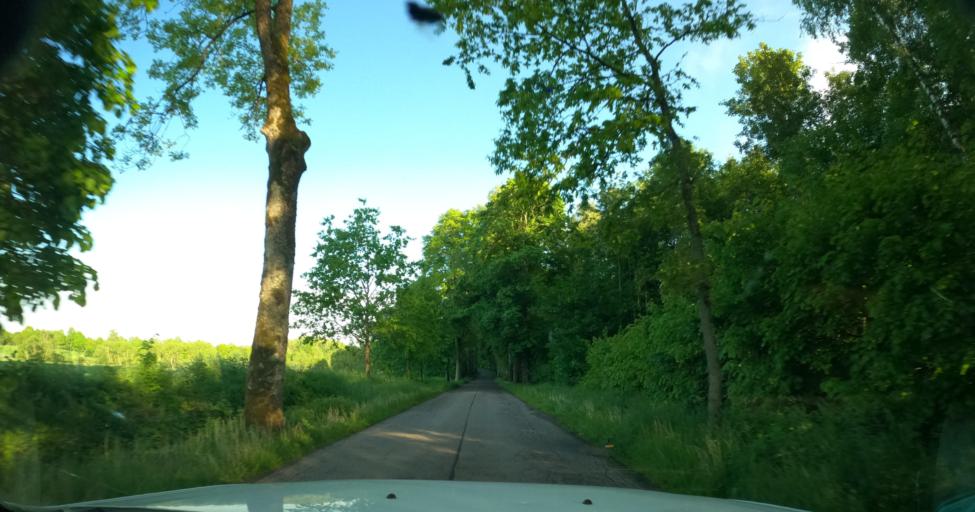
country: PL
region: Warmian-Masurian Voivodeship
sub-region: Powiat braniewski
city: Pieniezno
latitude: 54.2174
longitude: 20.0356
